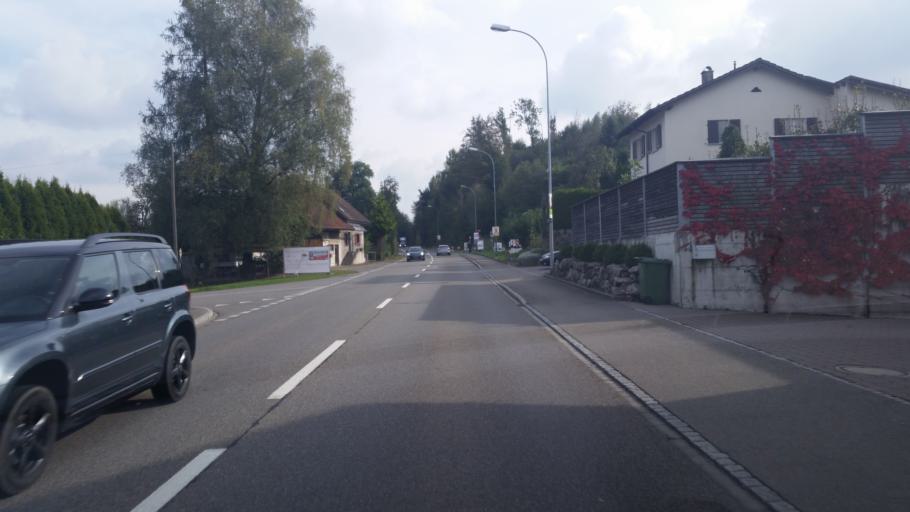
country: CH
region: Aargau
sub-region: Bezirk Baden
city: Kunten
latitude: 47.3660
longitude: 8.3144
